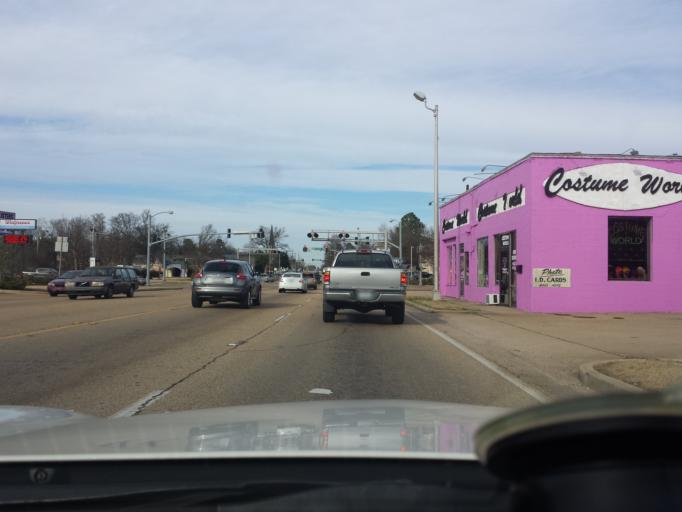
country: US
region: Mississippi
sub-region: Lee County
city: Tupelo
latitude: 34.2564
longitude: -88.7155
